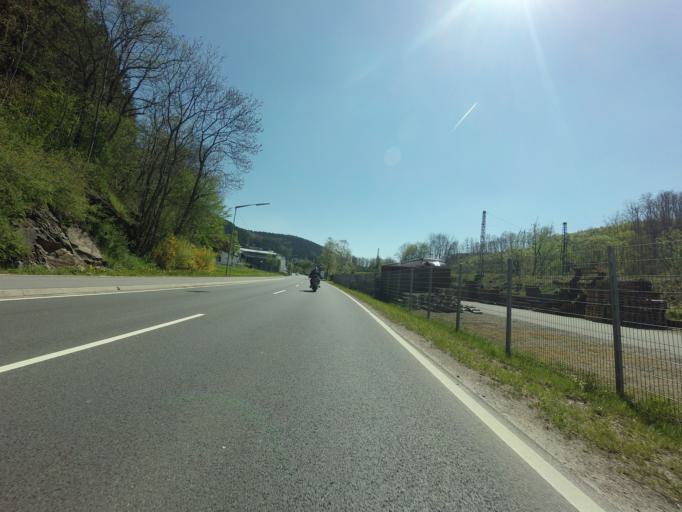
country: DE
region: North Rhine-Westphalia
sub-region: Regierungsbezirk Arnsberg
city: Lennestadt
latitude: 51.0916
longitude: 8.0731
